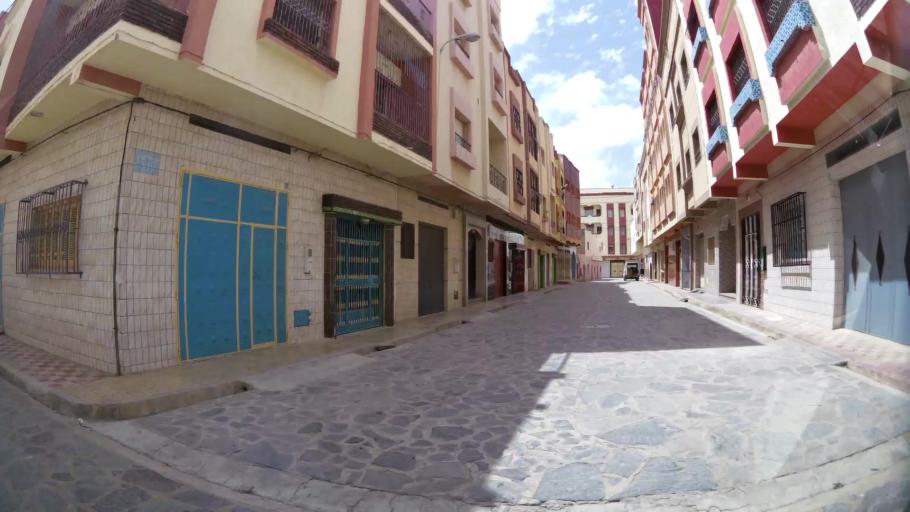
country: MA
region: Oriental
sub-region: Nador
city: Nador
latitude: 35.1643
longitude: -2.9272
